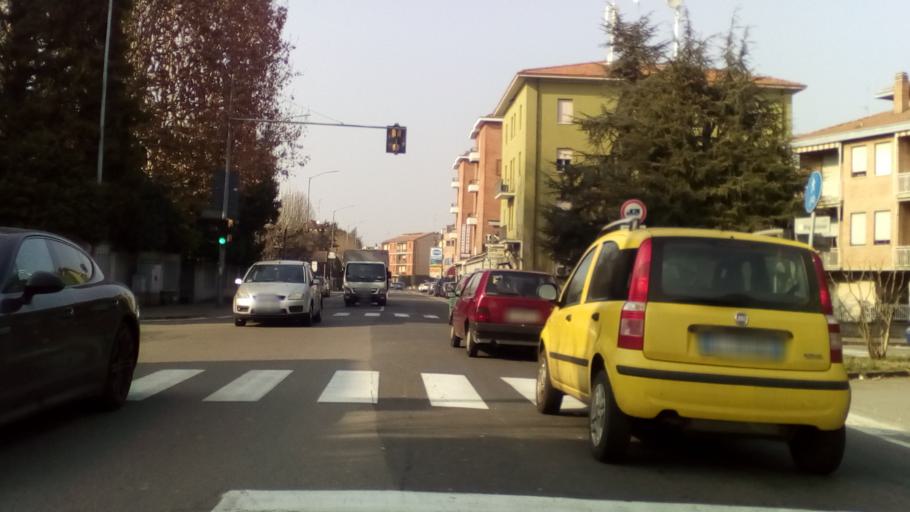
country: IT
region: Emilia-Romagna
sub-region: Provincia di Modena
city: Modena
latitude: 44.6303
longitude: 10.9418
